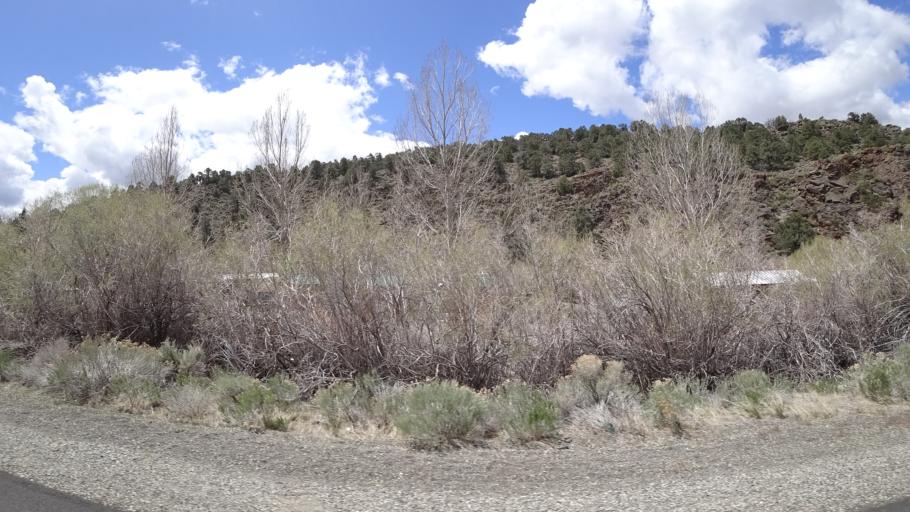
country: US
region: California
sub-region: Mono County
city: Bridgeport
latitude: 38.1879
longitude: -119.2045
